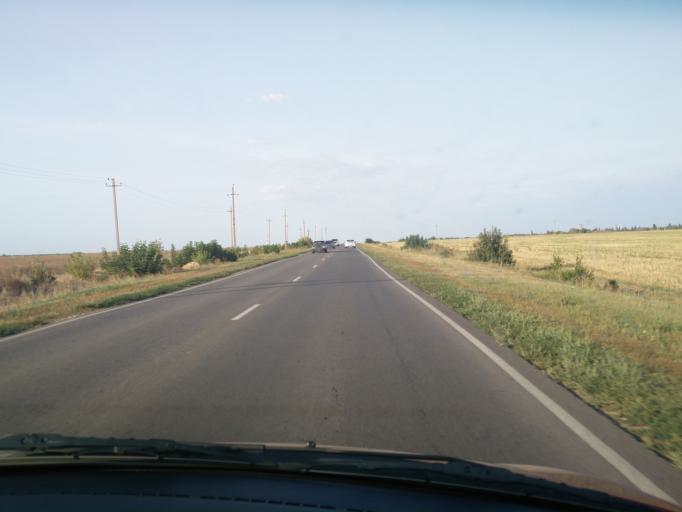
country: RU
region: Voronezj
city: Ramon'
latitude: 51.9295
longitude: 39.3284
